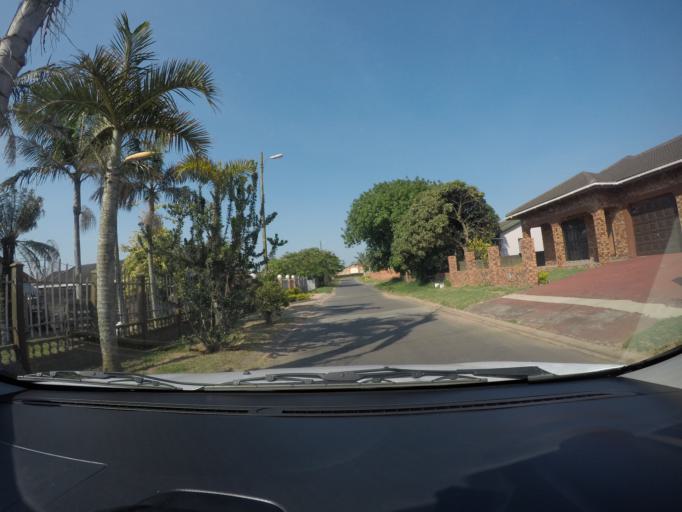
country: ZA
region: KwaZulu-Natal
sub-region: uThungulu District Municipality
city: Richards Bay
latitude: -28.7187
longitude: 32.0411
